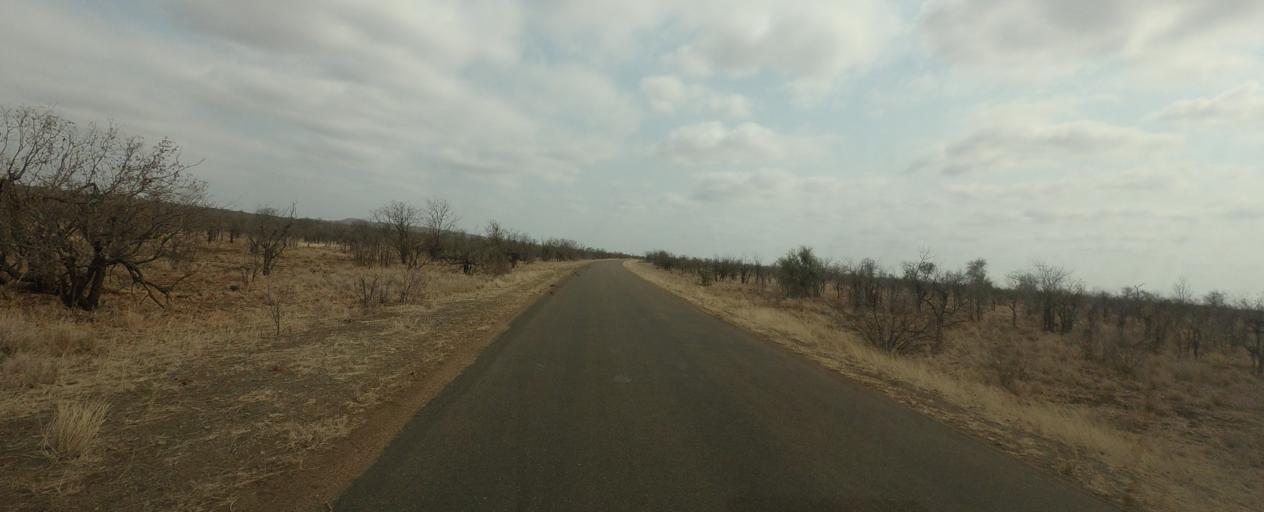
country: ZA
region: Limpopo
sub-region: Vhembe District Municipality
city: Mutale
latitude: -22.6176
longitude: 31.1747
